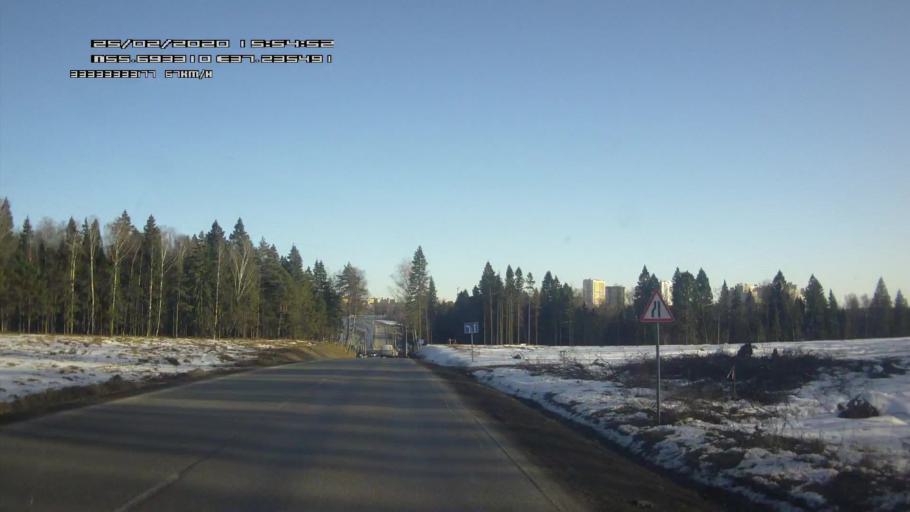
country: RU
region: Moskovskaya
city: Odintsovo
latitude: 55.6935
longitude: 37.2357
